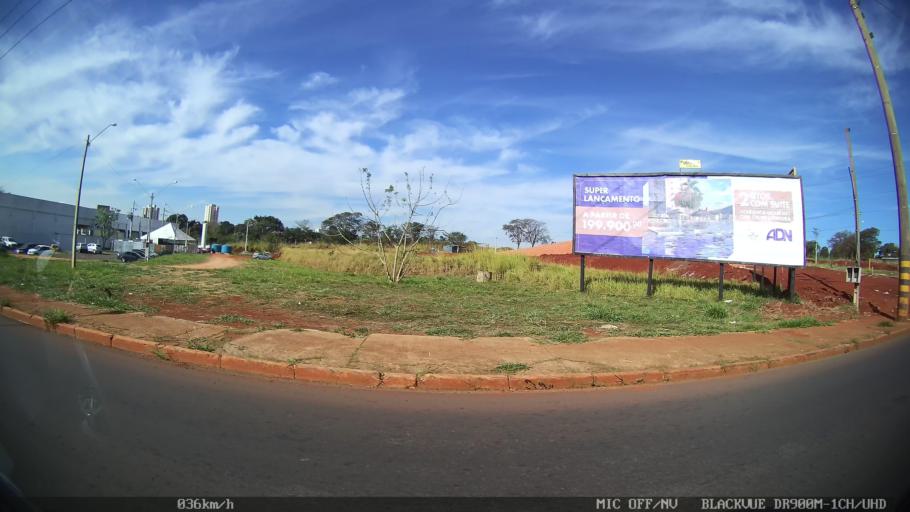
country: BR
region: Sao Paulo
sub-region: Araraquara
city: Araraquara
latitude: -21.8106
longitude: -48.1771
